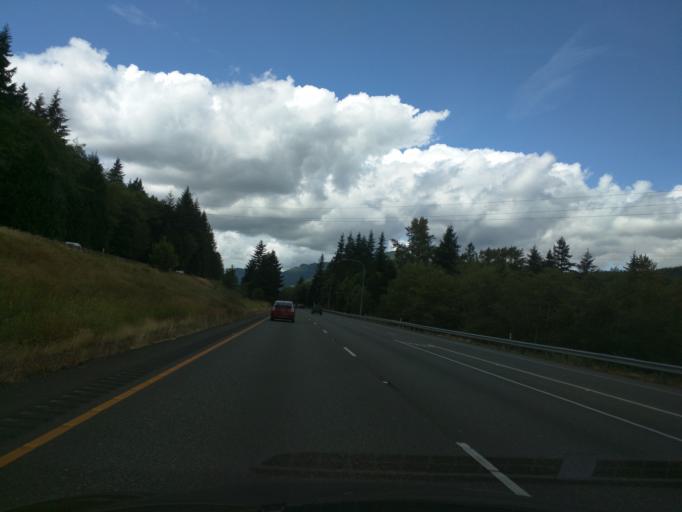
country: US
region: Washington
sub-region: Whatcom County
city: Sudden Valley
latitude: 48.6244
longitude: -122.3568
